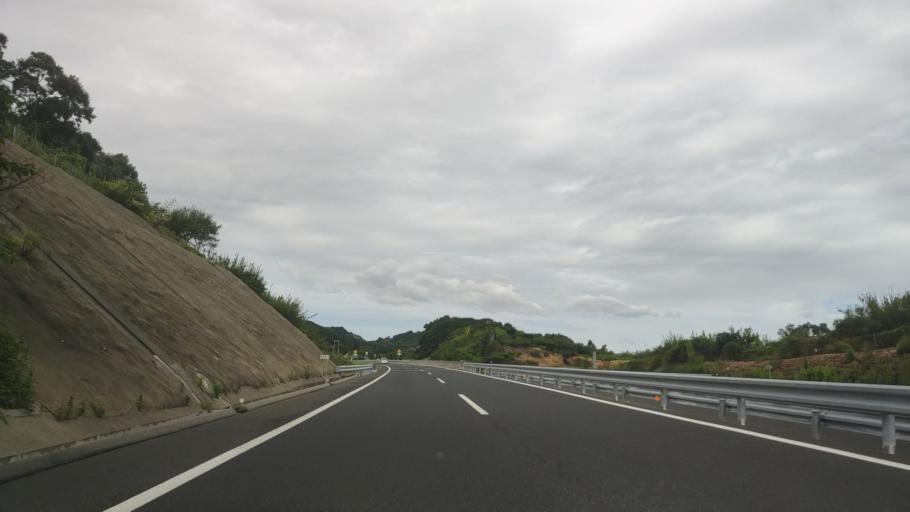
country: JP
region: Wakayama
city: Tanabe
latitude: 33.7622
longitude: 135.3526
